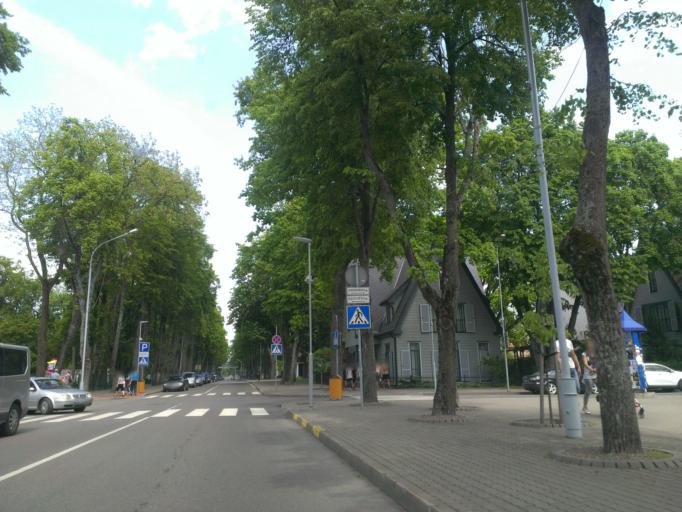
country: LT
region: Klaipedos apskritis
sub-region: Klaipeda
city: Palanga
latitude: 55.9131
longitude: 21.0639
